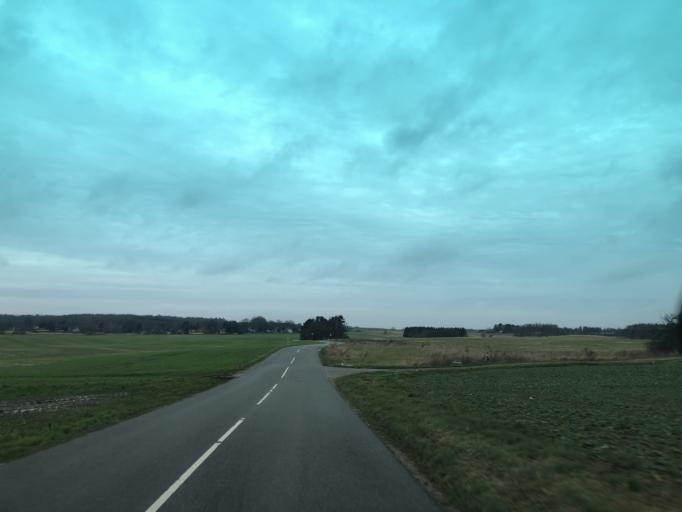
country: DK
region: Capital Region
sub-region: Allerod Kommune
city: Lynge
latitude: 55.8579
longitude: 12.2337
